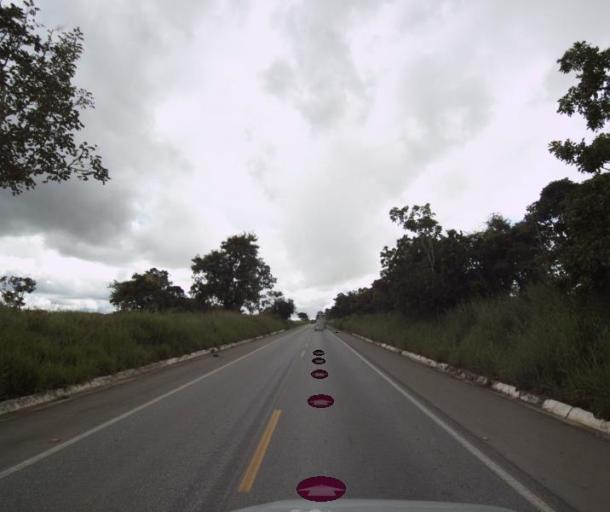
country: BR
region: Goias
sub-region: Uruacu
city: Uruacu
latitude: -14.2381
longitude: -49.1361
